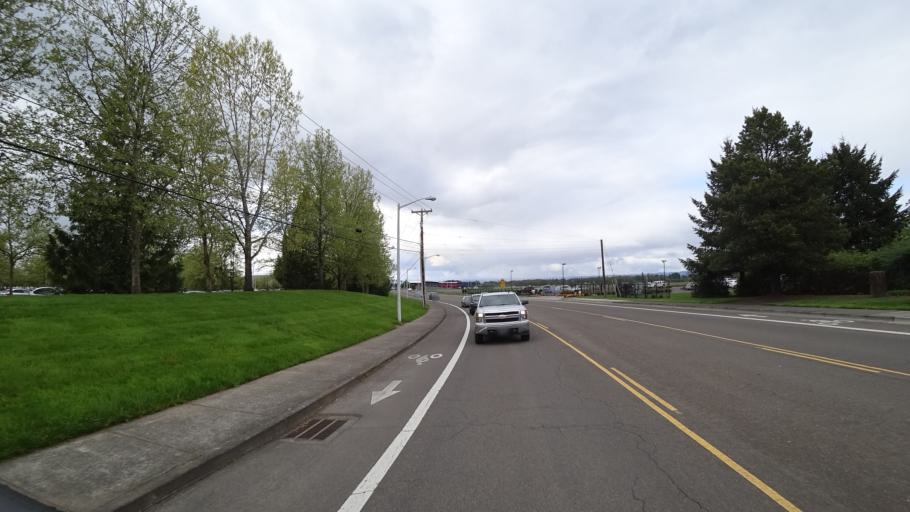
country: US
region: Oregon
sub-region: Washington County
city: Hillsboro
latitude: 45.5435
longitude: -122.9573
